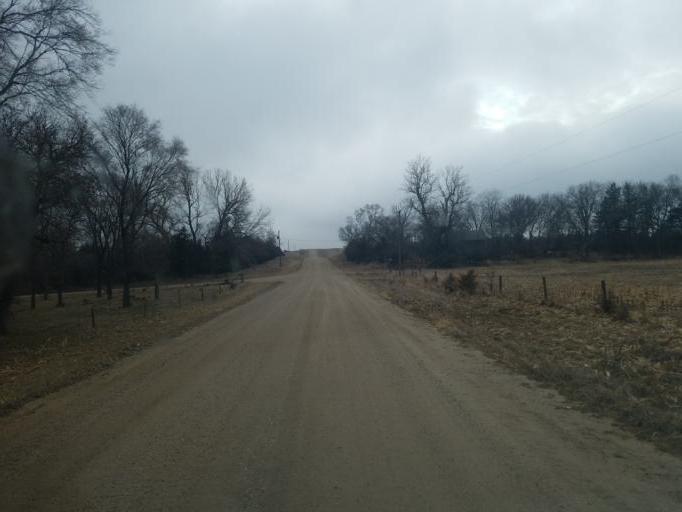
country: US
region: Nebraska
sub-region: Knox County
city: Center
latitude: 42.5256
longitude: -97.7990
